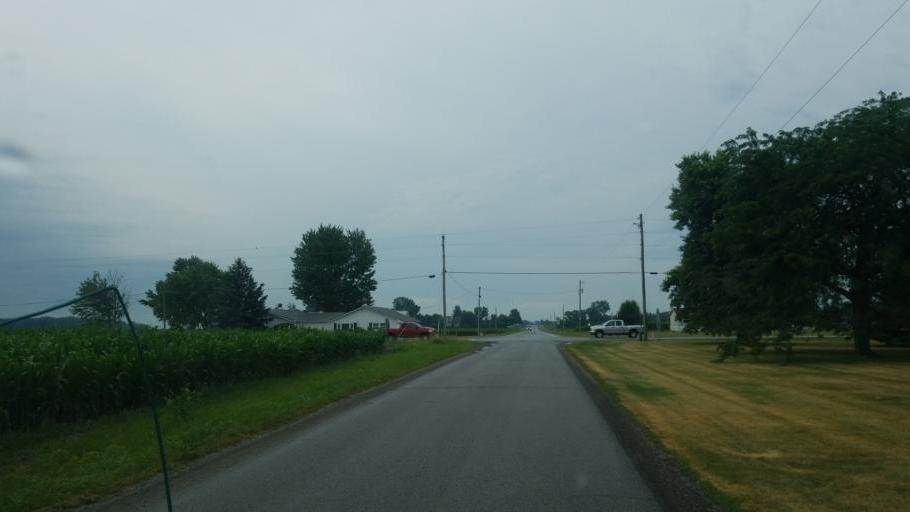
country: US
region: Ohio
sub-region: Williams County
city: Edgerton
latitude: 41.3839
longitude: -84.6698
